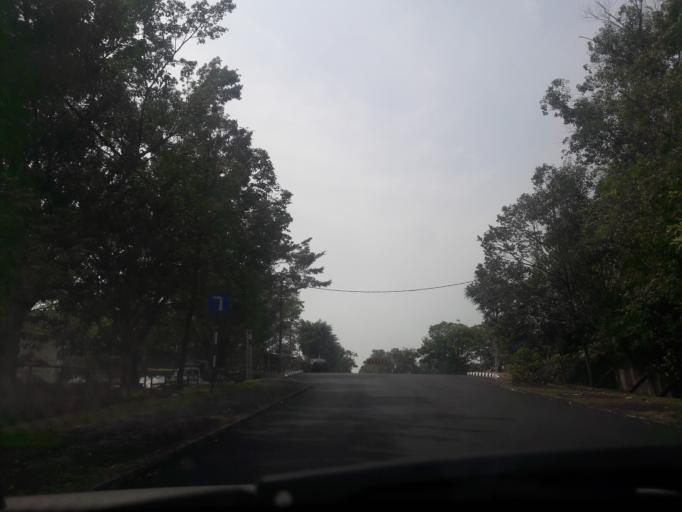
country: MY
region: Kedah
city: Kulim
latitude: 5.3694
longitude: 100.5640
